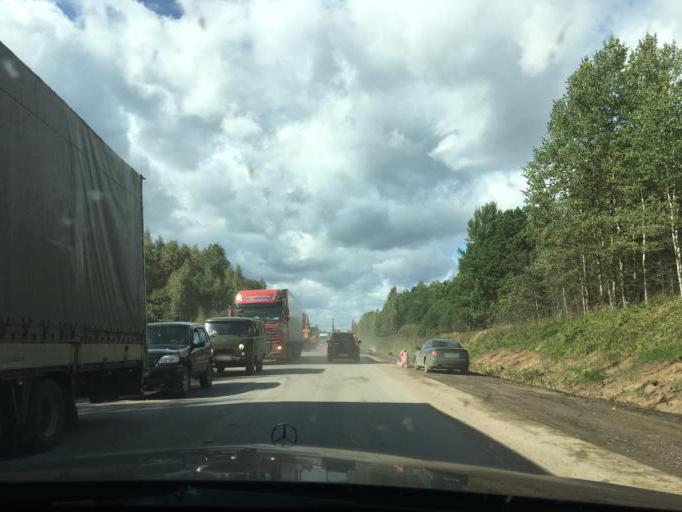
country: RU
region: Pskov
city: Novosokol'niki
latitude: 56.2815
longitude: 30.2964
